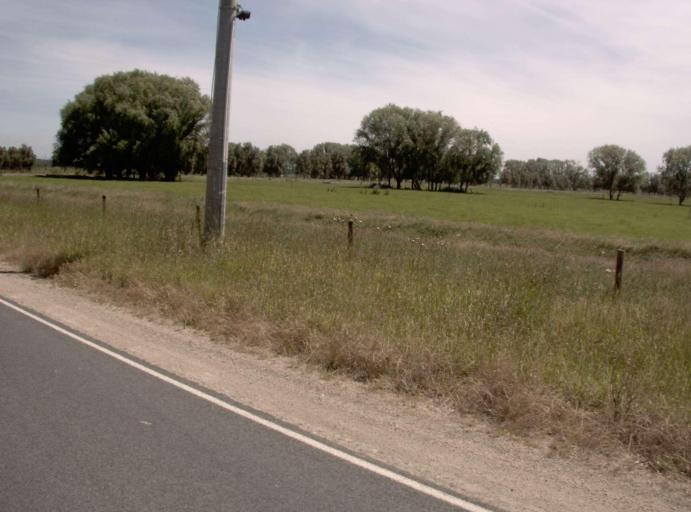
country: AU
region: Victoria
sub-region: Wellington
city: Heyfield
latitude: -38.0546
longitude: 146.8742
